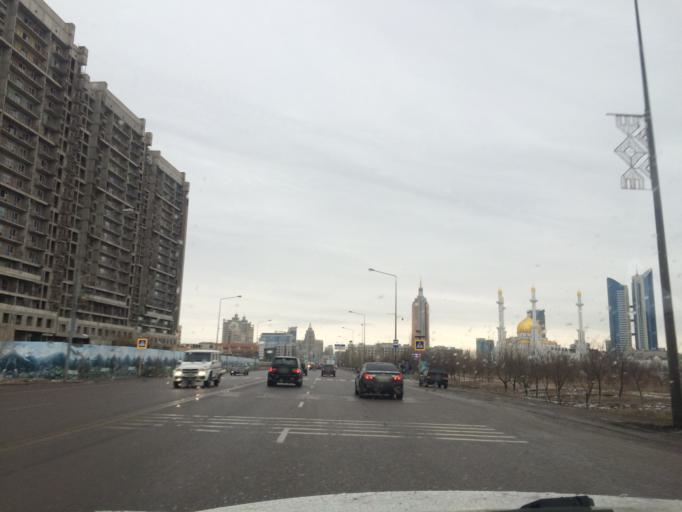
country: KZ
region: Astana Qalasy
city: Astana
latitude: 51.1226
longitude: 71.4126
